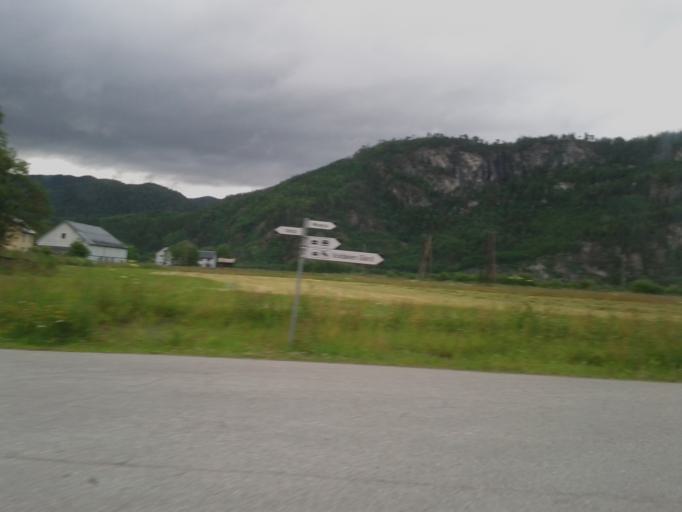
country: NO
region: Sor-Trondelag
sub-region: Midtre Gauldal
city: Storen
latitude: 63.0464
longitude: 10.2837
